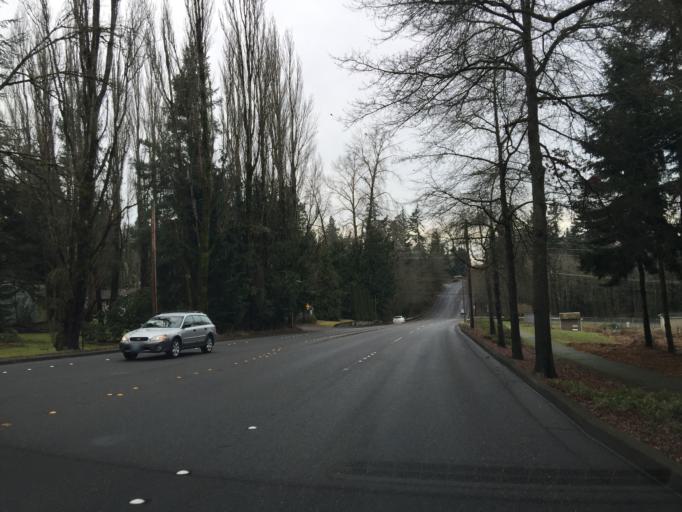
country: US
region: Washington
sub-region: Whatcom County
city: Geneva
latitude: 48.7455
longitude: -122.4429
